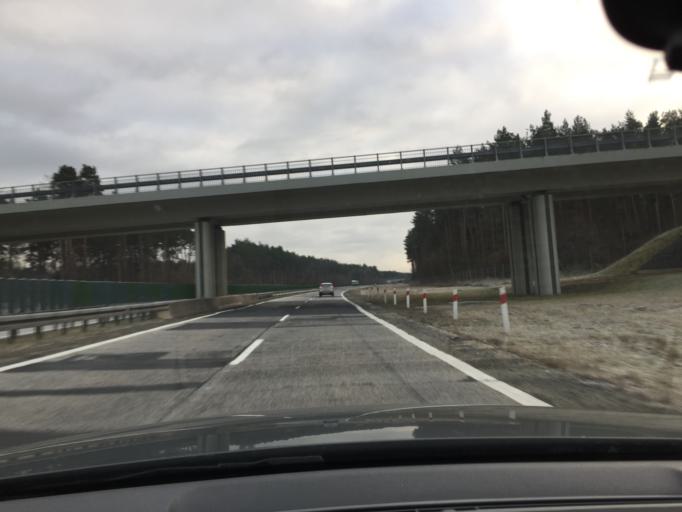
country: PL
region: Lubusz
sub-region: Powiat zarski
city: Lipinki Luzyckie
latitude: 51.6064
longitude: 14.9828
